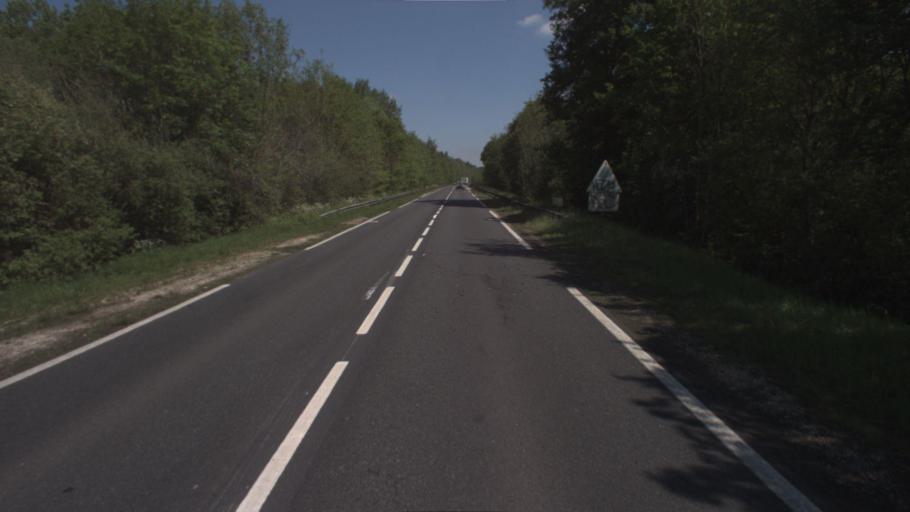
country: FR
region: Ile-de-France
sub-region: Departement de Seine-et-Marne
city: Chaumes-en-Brie
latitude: 48.6816
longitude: 2.8148
